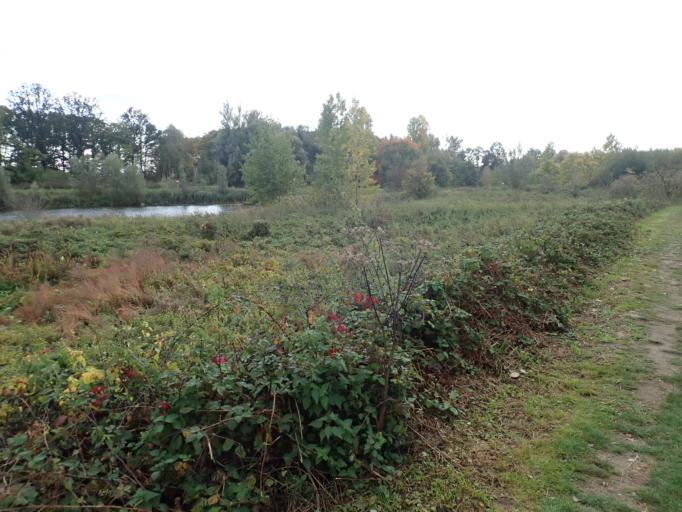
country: BE
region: Flanders
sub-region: Provincie Oost-Vlaanderen
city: Kruibeke
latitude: 51.1552
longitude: 4.3146
